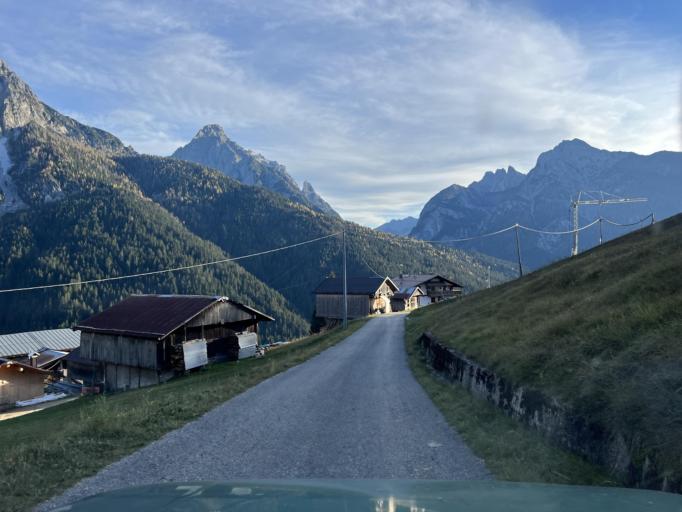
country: IT
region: Veneto
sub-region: Provincia di Belluno
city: San Pietro di Cadore
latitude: 46.5796
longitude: 12.5961
